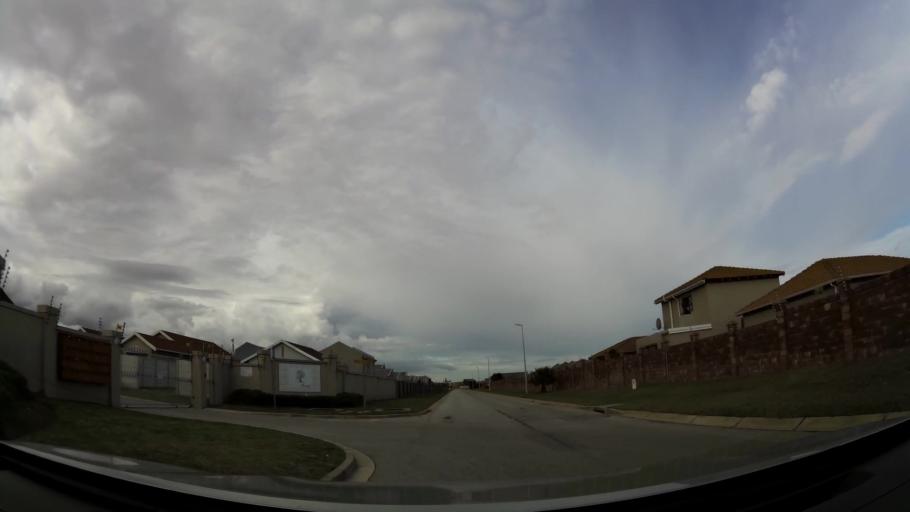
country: ZA
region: Eastern Cape
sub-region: Nelson Mandela Bay Metropolitan Municipality
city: Port Elizabeth
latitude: -33.9317
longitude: 25.4662
